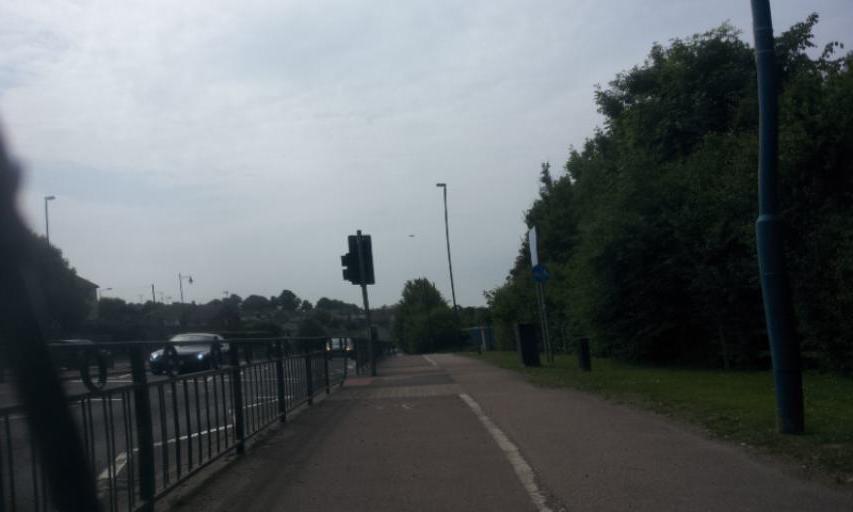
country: GB
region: England
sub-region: Kent
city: Gillingham
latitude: 51.3909
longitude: 0.5734
